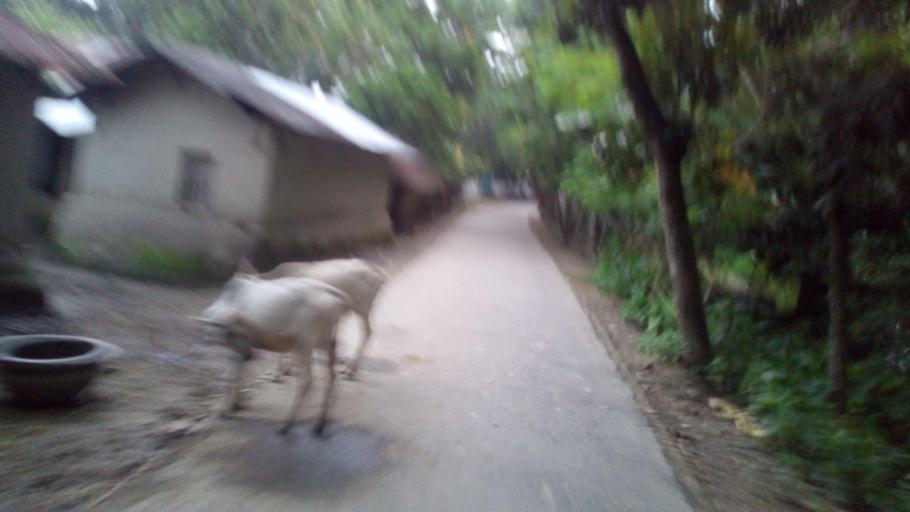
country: BD
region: Khulna
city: Phultala
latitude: 22.7588
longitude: 89.4081
